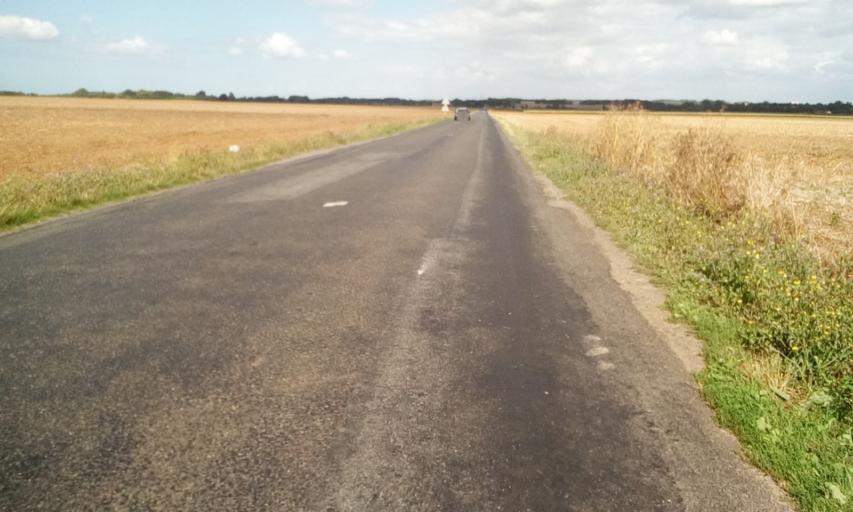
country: FR
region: Lower Normandy
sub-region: Departement du Calvados
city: Bellengreville
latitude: 49.0939
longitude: -0.2107
